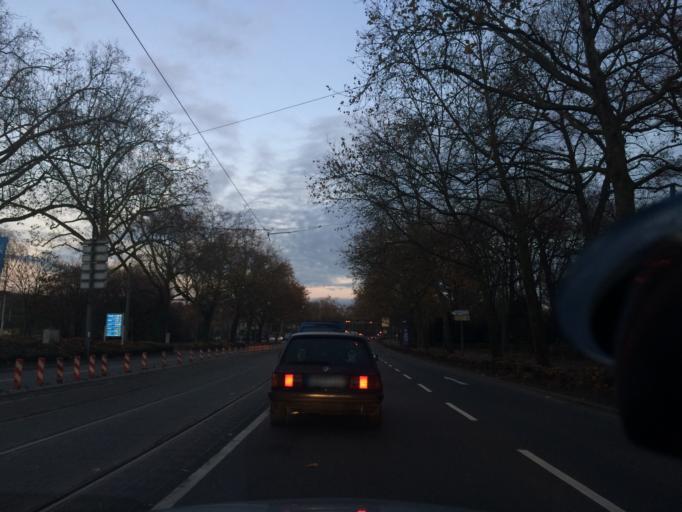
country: DE
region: Hesse
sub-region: Regierungsbezirk Darmstadt
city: Frankfurt am Main
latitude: 50.1231
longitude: 8.7231
